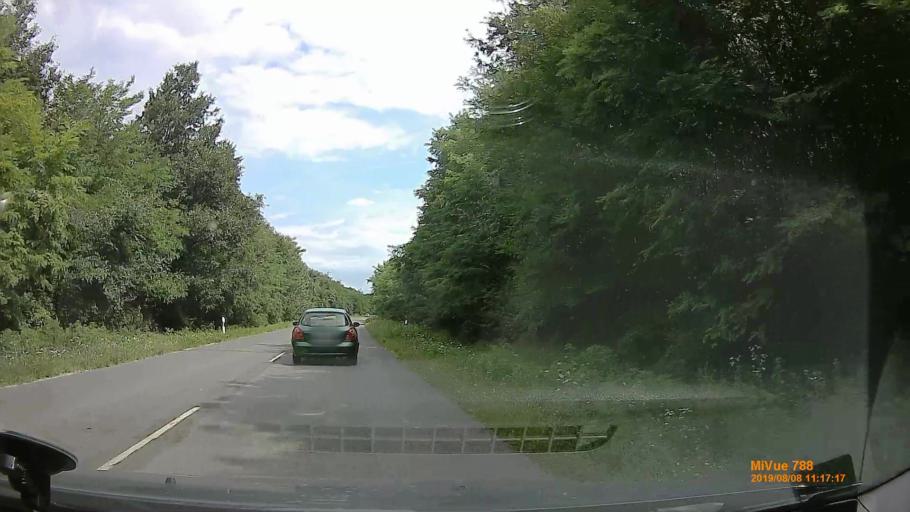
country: HU
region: Somogy
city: Balatonbereny
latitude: 46.6573
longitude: 17.3162
